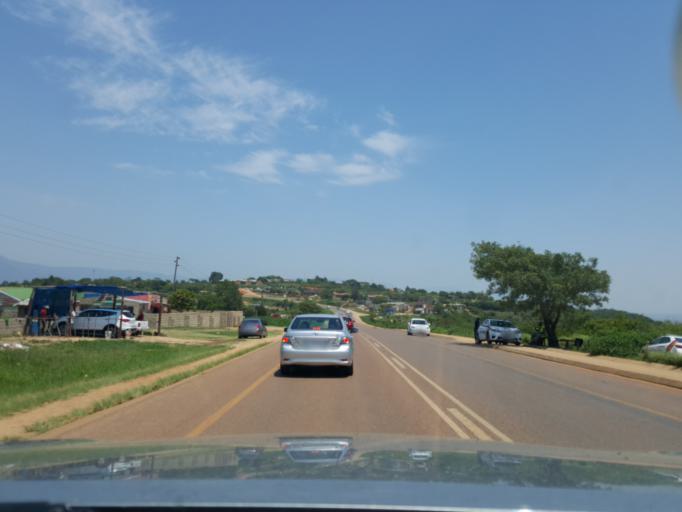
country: ZA
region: Limpopo
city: Thulamahashi
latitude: -24.8473
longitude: 31.1011
